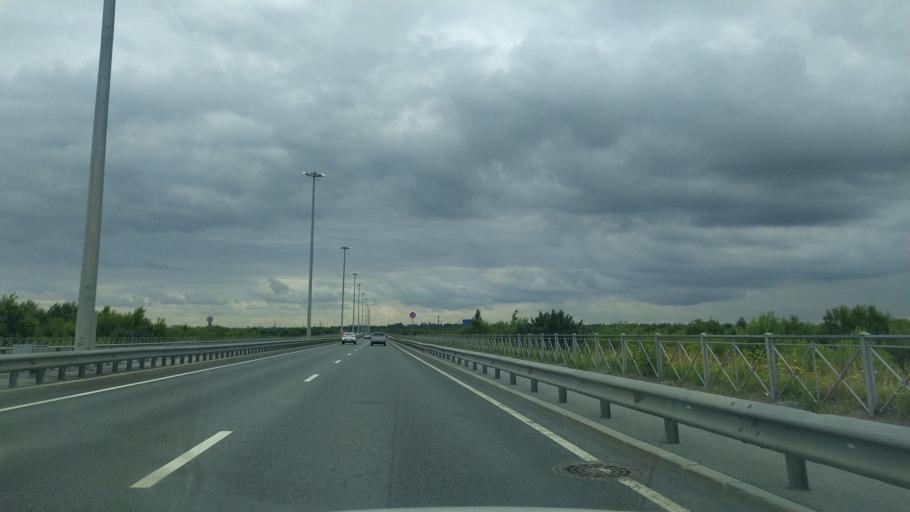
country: RU
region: St.-Petersburg
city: Pushkin
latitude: 59.7607
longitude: 30.3938
